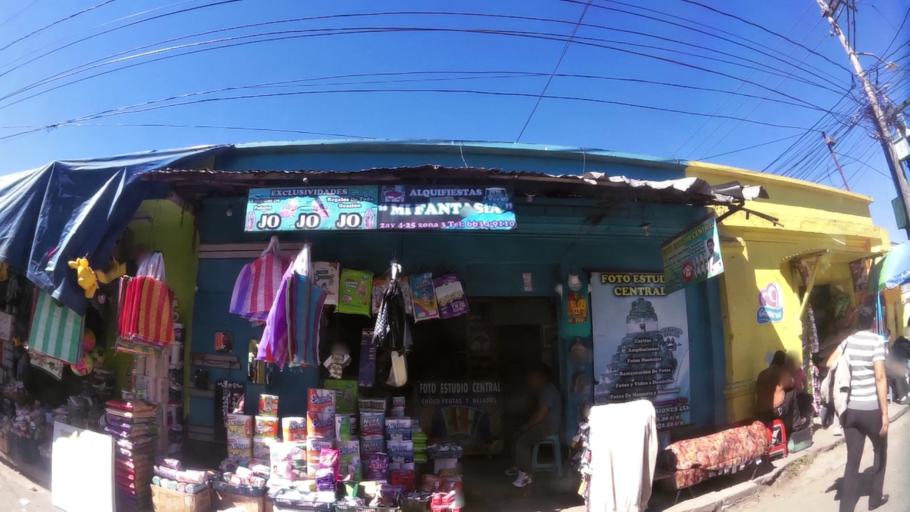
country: GT
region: Guatemala
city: San Jose Pinula
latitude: 14.5459
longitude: -90.4128
